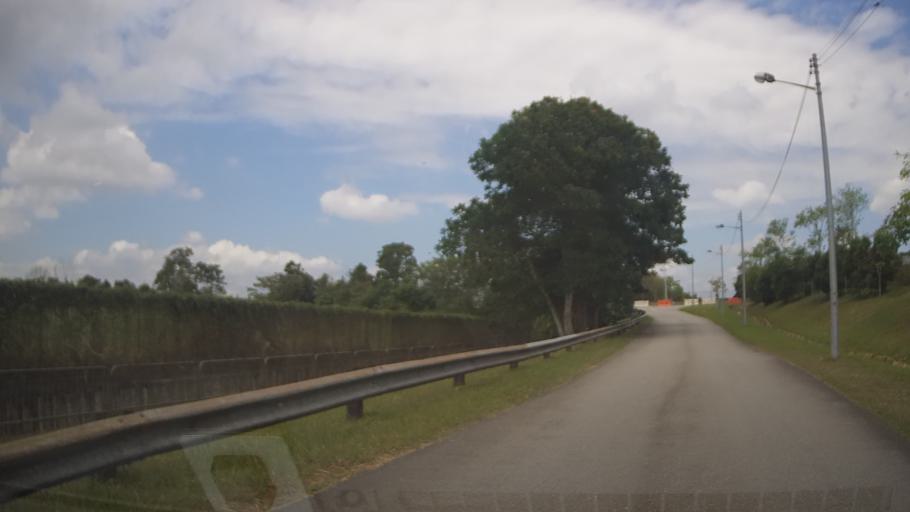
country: MY
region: Johor
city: Johor Bahru
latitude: 1.4244
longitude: 103.7218
